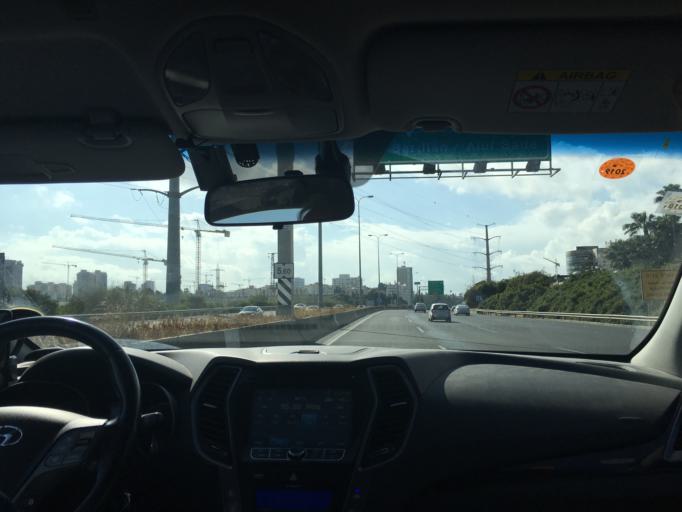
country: IL
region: Tel Aviv
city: Giv`at Shemu'el
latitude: 32.0868
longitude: 34.8457
